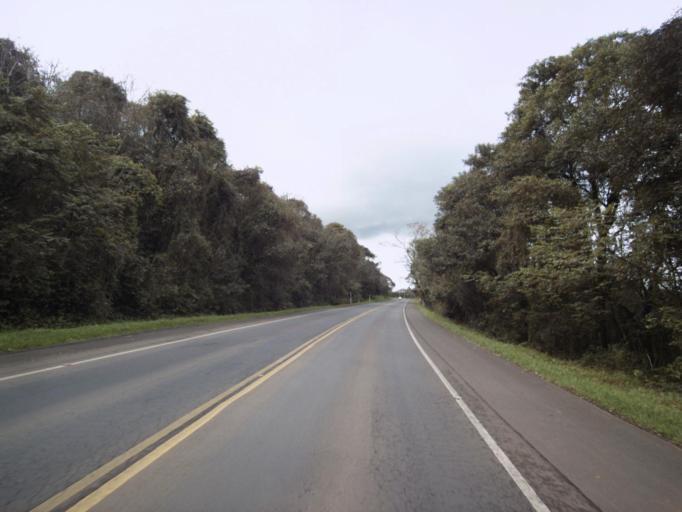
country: BR
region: Santa Catarina
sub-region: Concordia
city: Concordia
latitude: -27.2636
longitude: -51.9582
